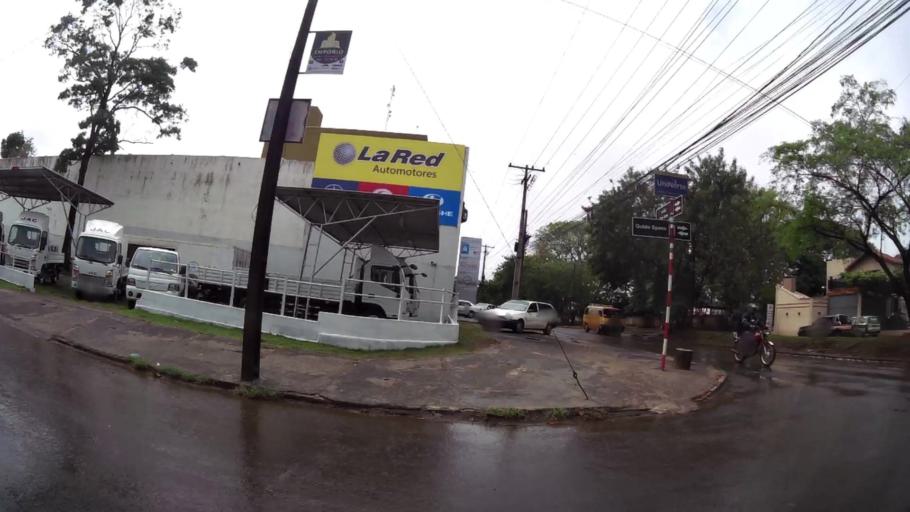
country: PY
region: Alto Parana
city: Presidente Franco
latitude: -25.5150
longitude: -54.6455
